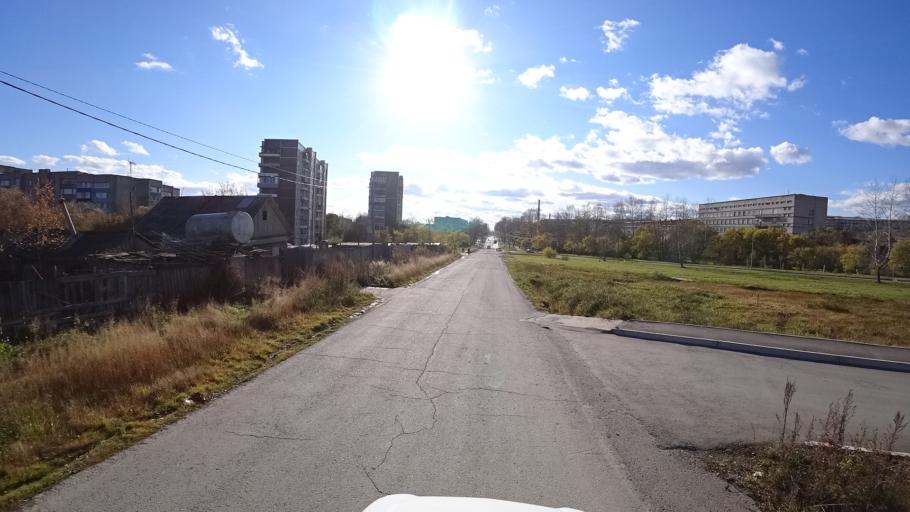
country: RU
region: Khabarovsk Krai
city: Amursk
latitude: 50.2347
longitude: 136.9122
